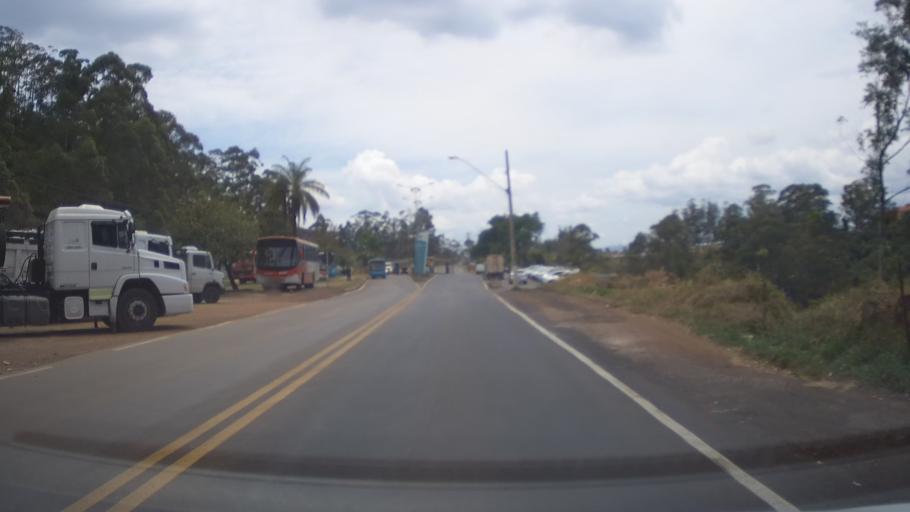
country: BR
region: Minas Gerais
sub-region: Belo Horizonte
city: Belo Horizonte
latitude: -19.9686
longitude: -43.9188
